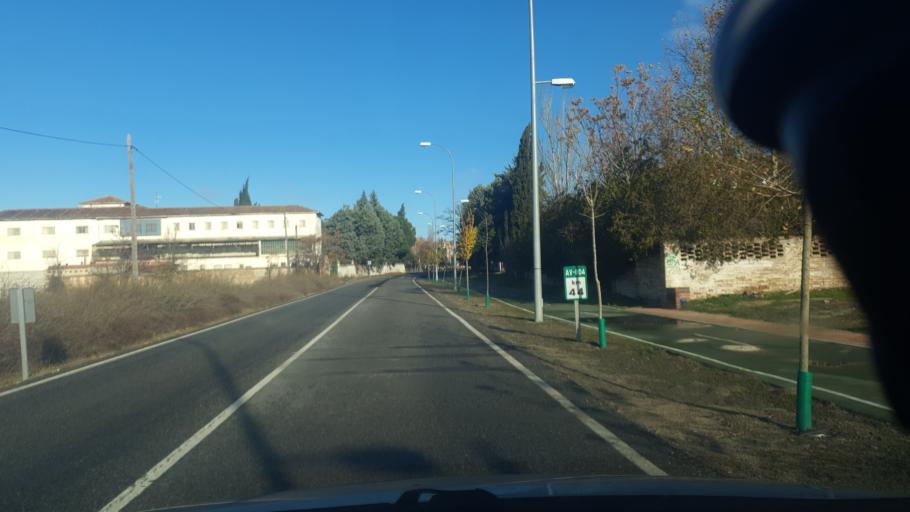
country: ES
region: Castille and Leon
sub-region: Provincia de Avila
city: Arevalo
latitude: 41.0514
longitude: -4.7192
